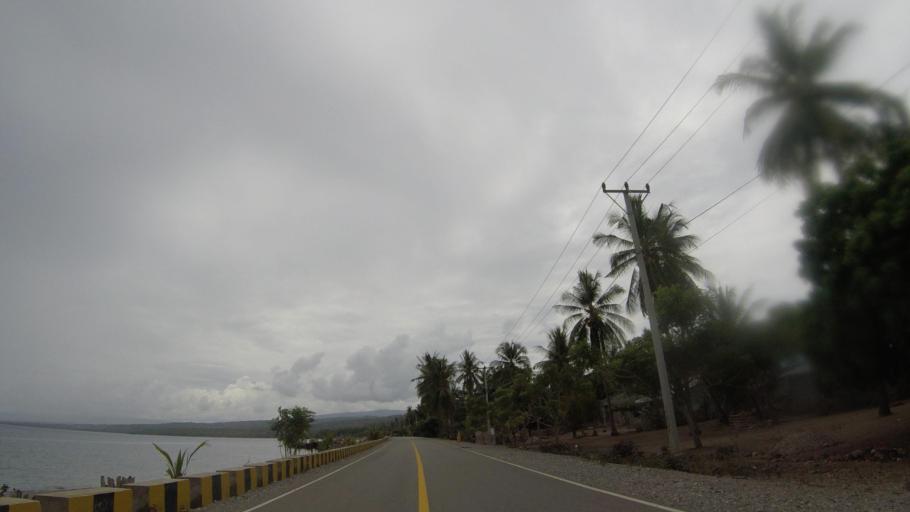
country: TL
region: Lautem
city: Lospalos
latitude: -8.4182
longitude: 126.7517
